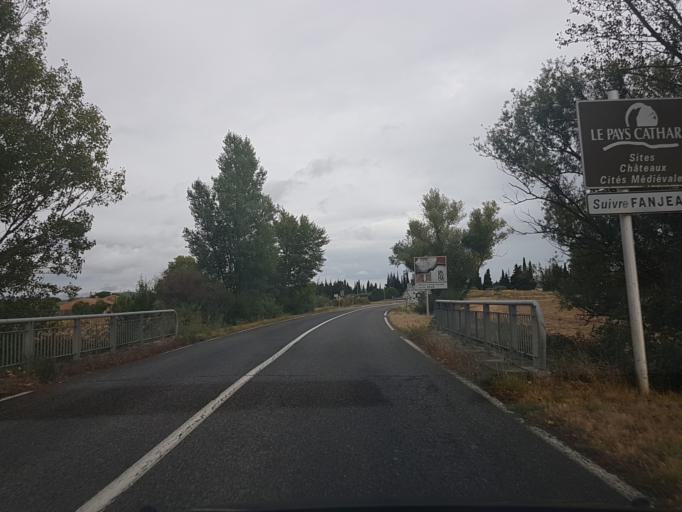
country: FR
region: Languedoc-Roussillon
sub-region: Departement de l'Aude
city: Bram
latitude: 43.2394
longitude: 2.1032
